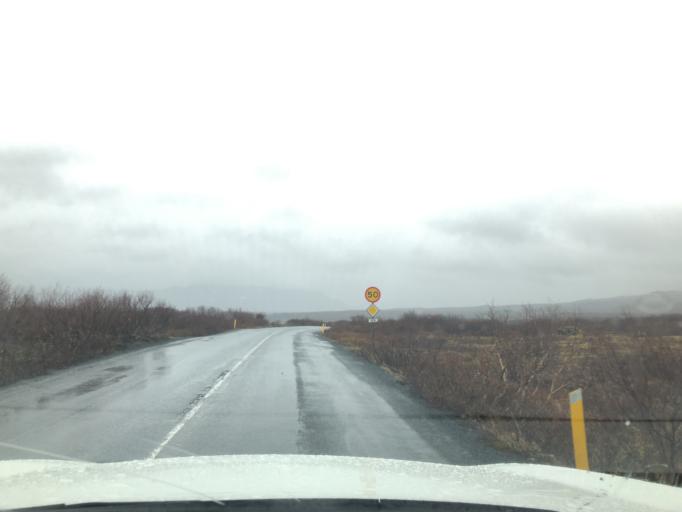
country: IS
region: South
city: Hveragerdi
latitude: 64.2280
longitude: -21.0522
